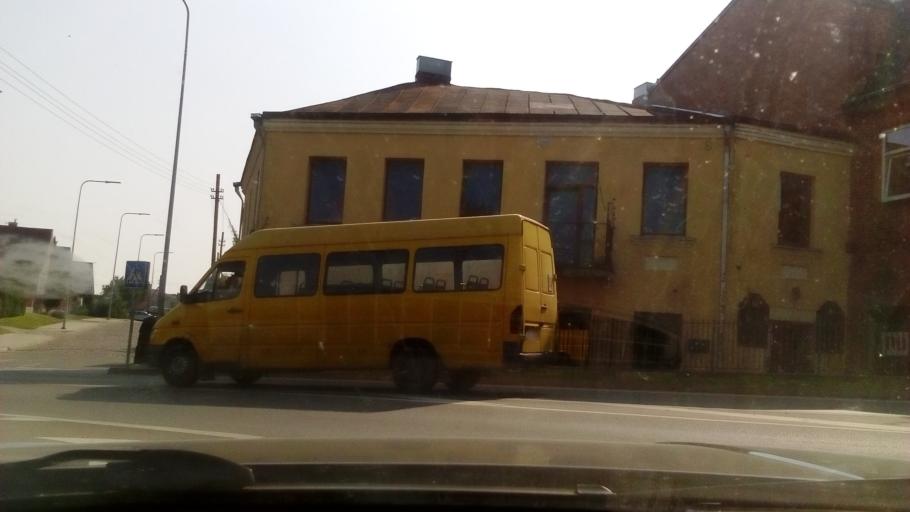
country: LT
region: Alytaus apskritis
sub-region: Alytus
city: Alytus
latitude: 54.4004
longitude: 24.0501
